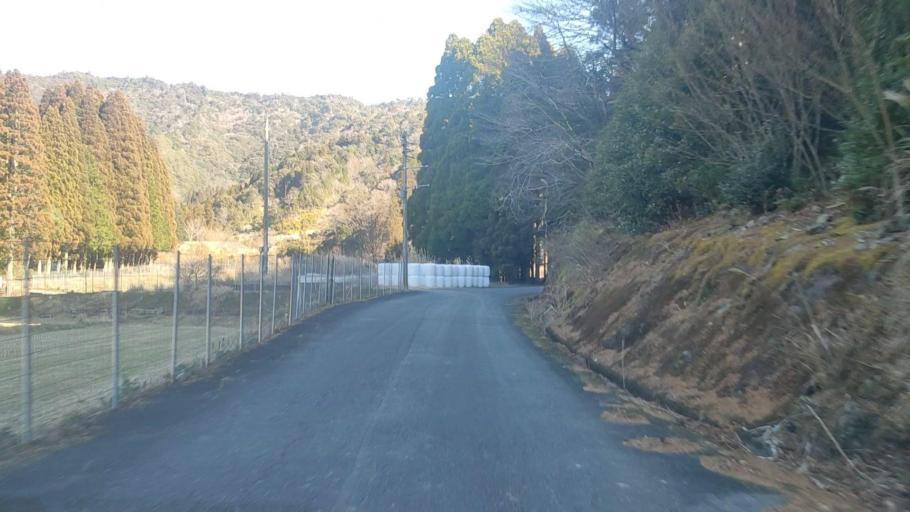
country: JP
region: Oita
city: Saiki
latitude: 32.7805
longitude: 131.8338
